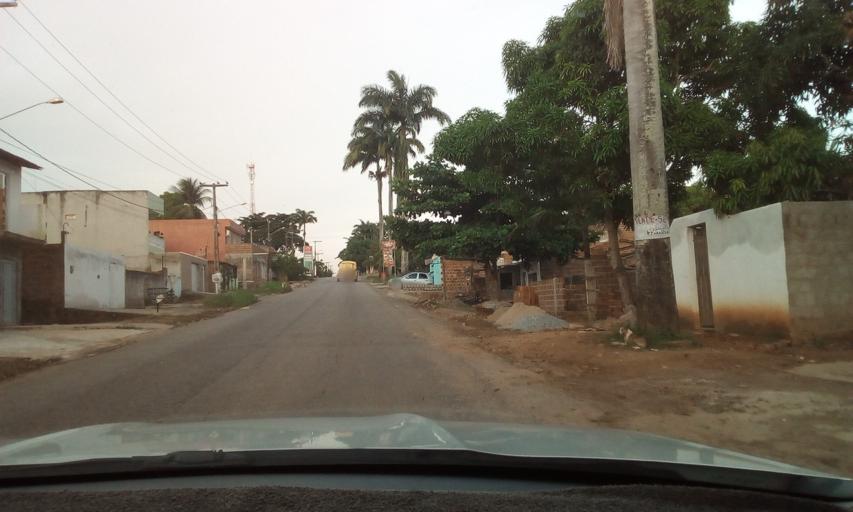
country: BR
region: Pernambuco
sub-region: Vicencia
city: Vicencia
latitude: -7.5997
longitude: -35.2351
